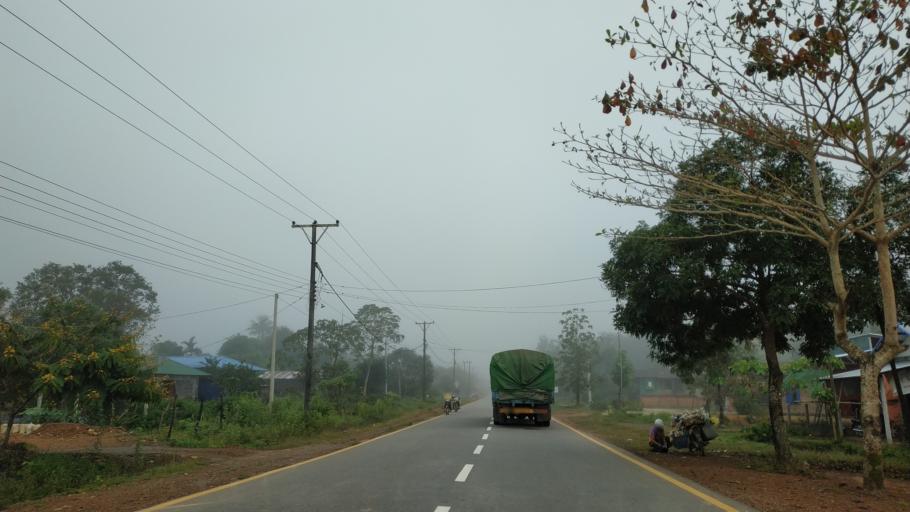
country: MM
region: Tanintharyi
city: Dawei
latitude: 14.1837
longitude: 98.2082
